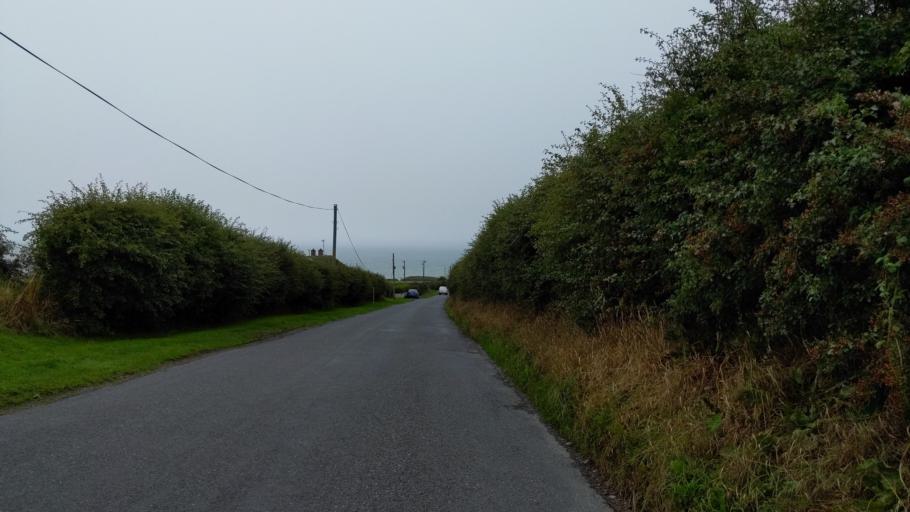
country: IE
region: Leinster
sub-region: Lu
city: Clogherhead
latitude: 53.7937
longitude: -6.2287
